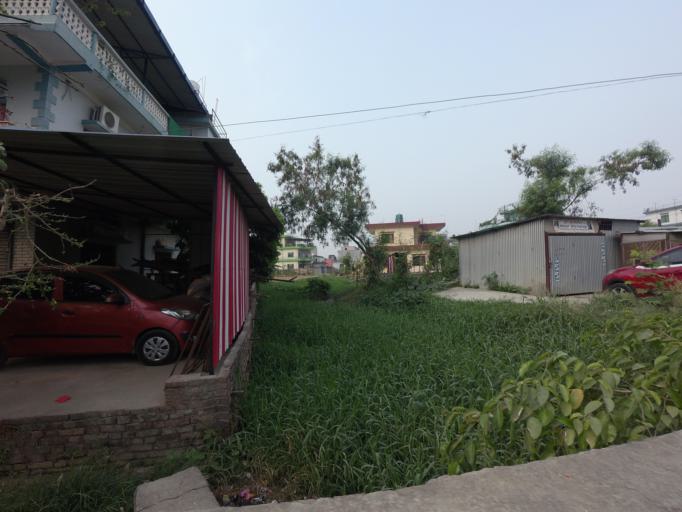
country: NP
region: Western Region
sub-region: Lumbini Zone
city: Bhairahawa
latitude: 27.5206
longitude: 83.4415
